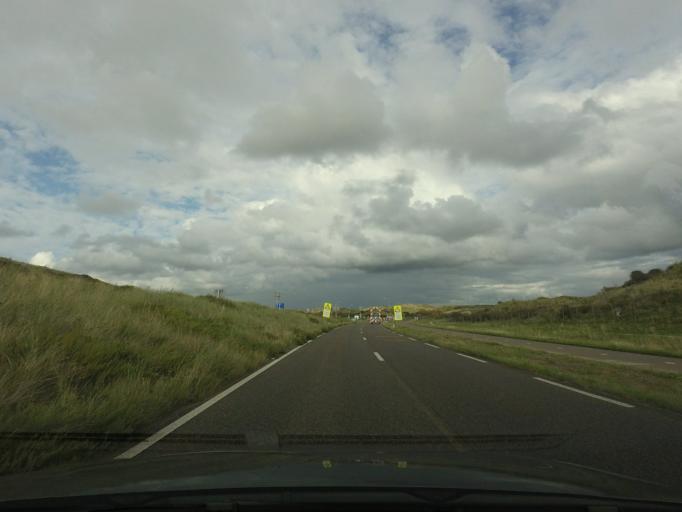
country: NL
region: North Holland
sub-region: Gemeente Zandvoort
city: Zandvoort
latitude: 52.4036
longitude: 4.5494
